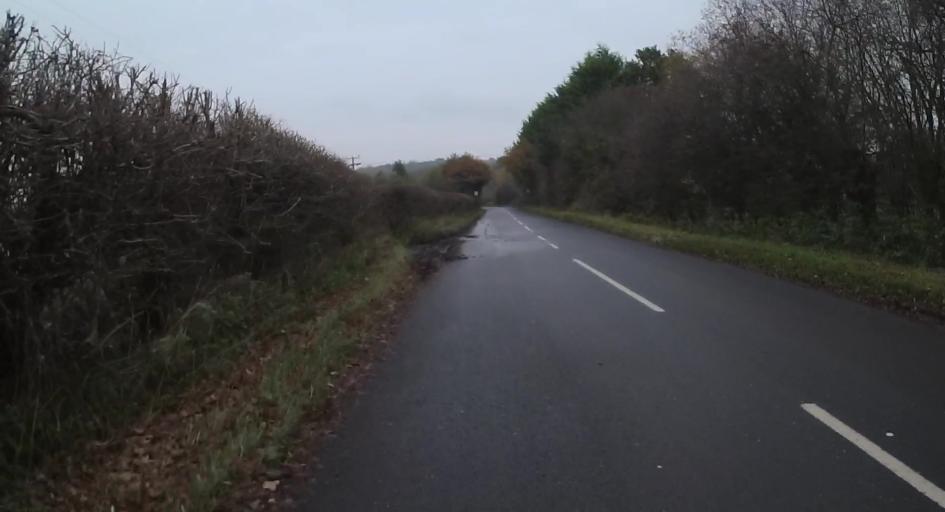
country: GB
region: England
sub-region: Hampshire
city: Kingsley
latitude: 51.1658
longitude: -0.8637
